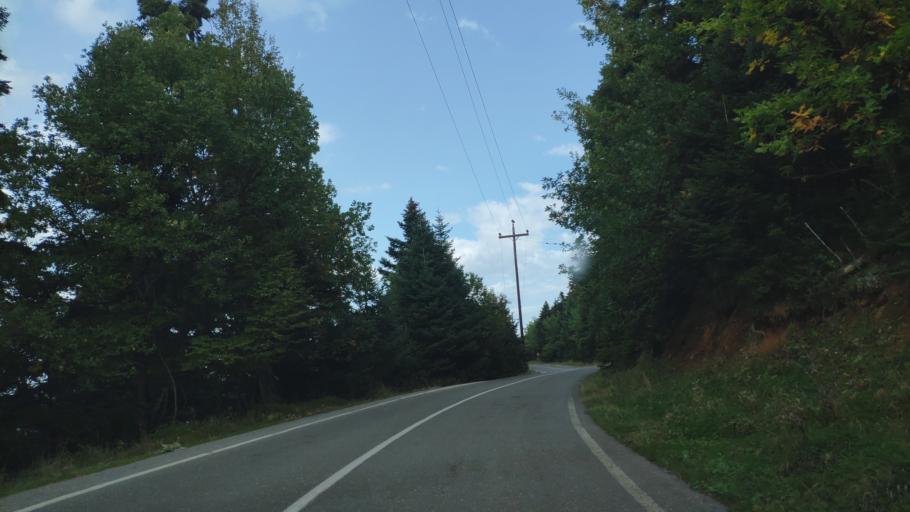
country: GR
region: Central Greece
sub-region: Nomos Fthiotidos
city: Anthili
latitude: 38.7369
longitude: 22.3712
